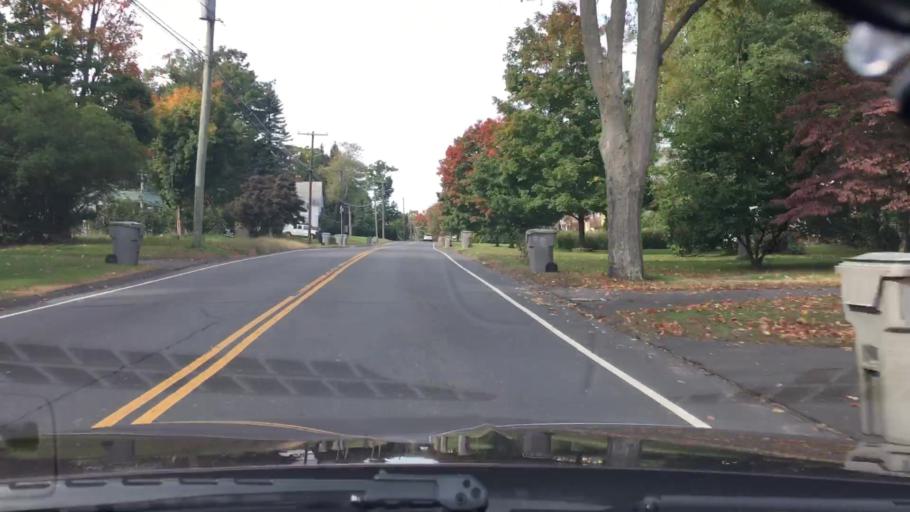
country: US
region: Connecticut
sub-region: Hartford County
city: Plainville
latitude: 41.6779
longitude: -72.8909
